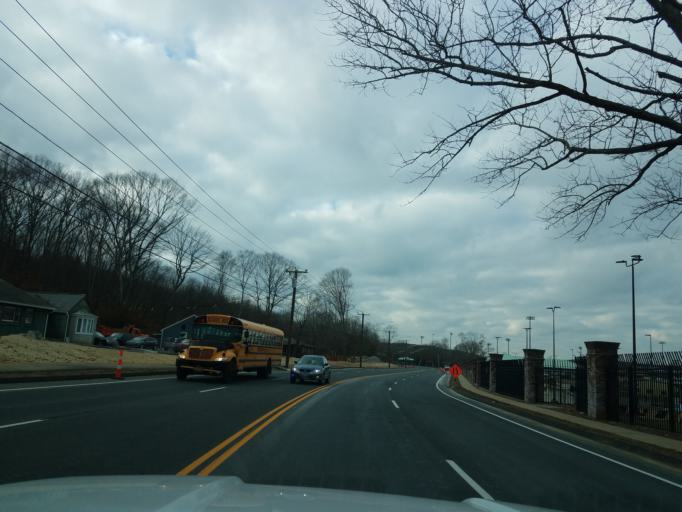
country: US
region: Connecticut
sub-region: New London County
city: Conning Towers-Nautilus Park
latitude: 41.3873
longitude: -72.0806
